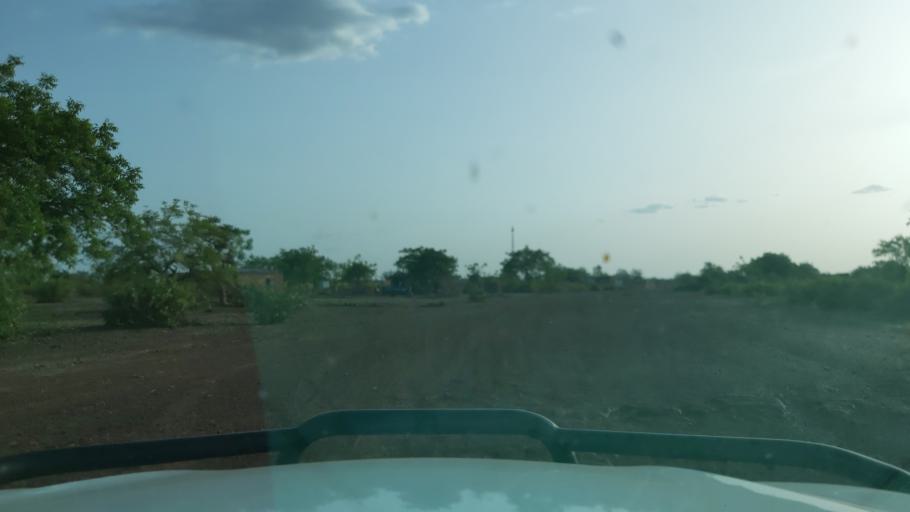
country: ML
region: Koulikoro
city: Kolokani
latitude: 13.2042
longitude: -7.9248
